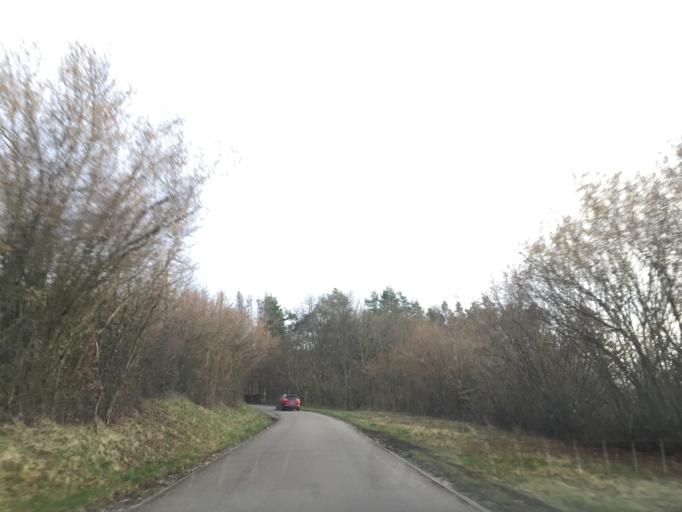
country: BE
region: Wallonia
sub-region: Province du Luxembourg
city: Hotton
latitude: 50.3034
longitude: 5.4945
